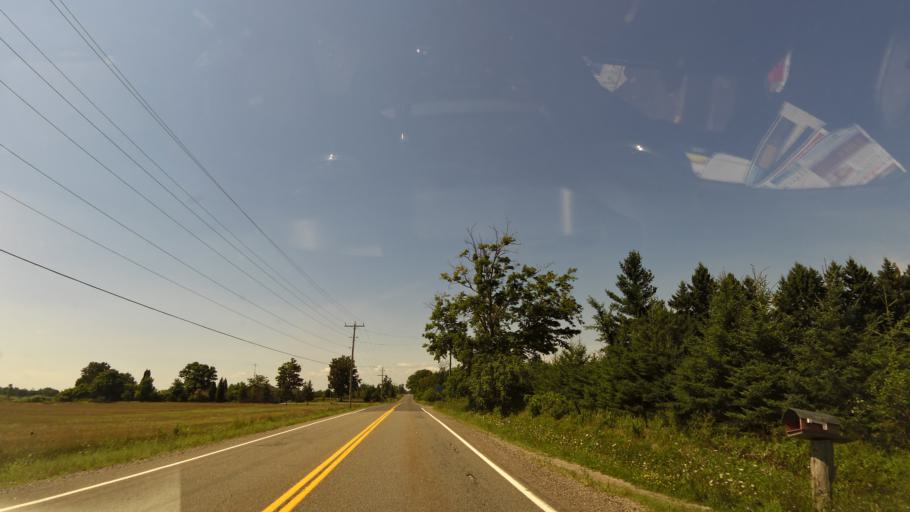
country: CA
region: Ontario
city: Ancaster
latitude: 43.1680
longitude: -79.9636
